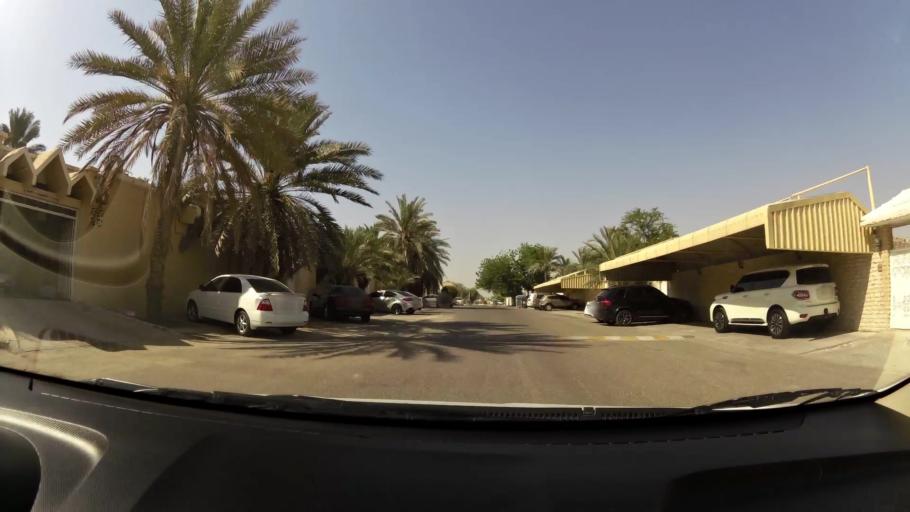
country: AE
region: Ajman
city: Ajman
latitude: 25.4079
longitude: 55.4679
